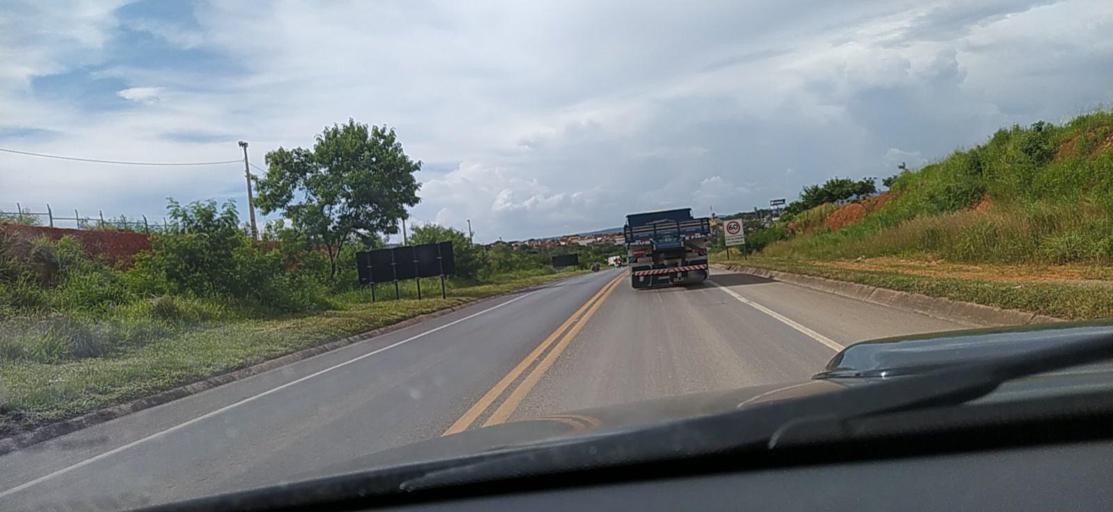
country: BR
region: Minas Gerais
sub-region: Montes Claros
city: Montes Claros
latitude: -16.7557
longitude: -43.8448
